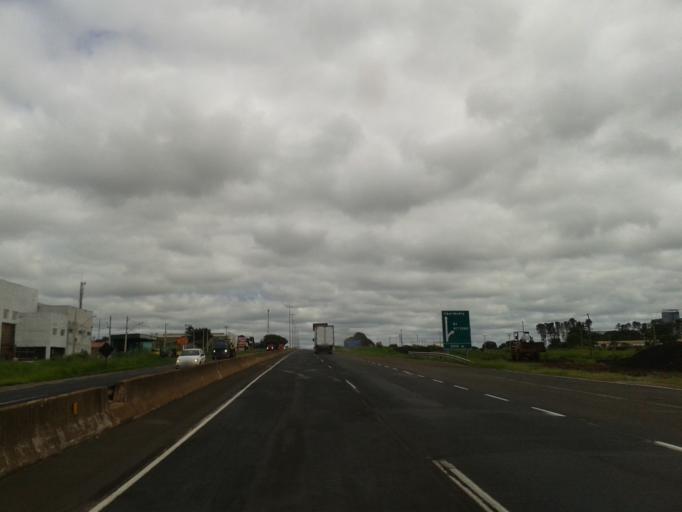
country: BR
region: Minas Gerais
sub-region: Uberaba
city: Uberaba
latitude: -19.7172
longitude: -47.9804
